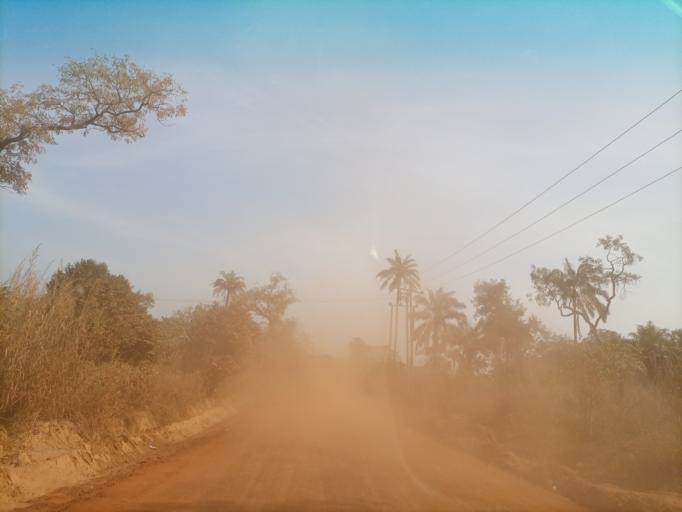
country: NG
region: Enugu
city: Eha Amufu
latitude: 6.6665
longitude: 7.7539
